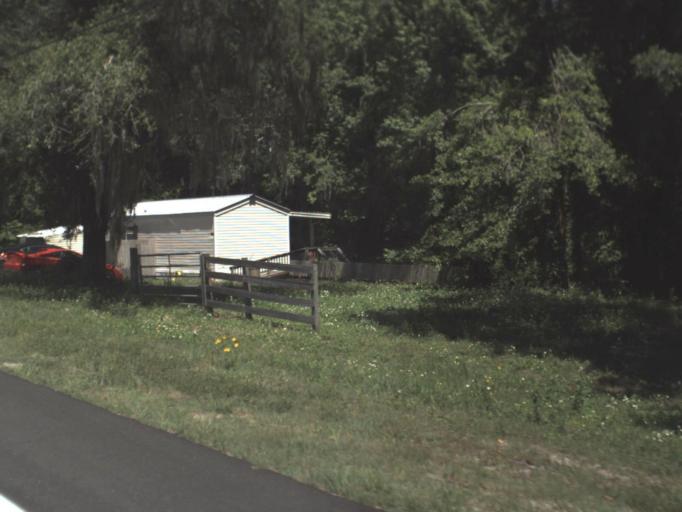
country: US
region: Florida
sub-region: Suwannee County
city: Wellborn
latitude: 30.2024
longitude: -82.7858
